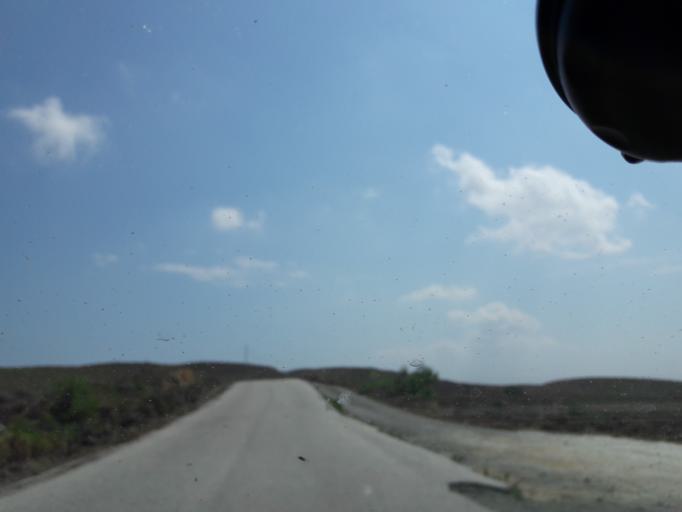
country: GR
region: North Aegean
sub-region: Nomos Lesvou
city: Myrina
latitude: 39.9777
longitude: 25.3504
